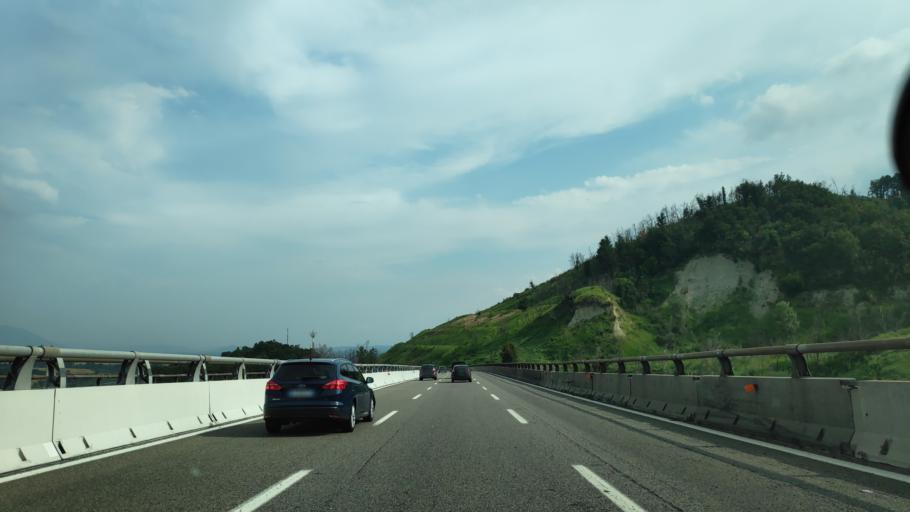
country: IT
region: Latium
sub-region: Citta metropolitana di Roma Capitale
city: Nazzano
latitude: 42.2121
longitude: 12.6010
